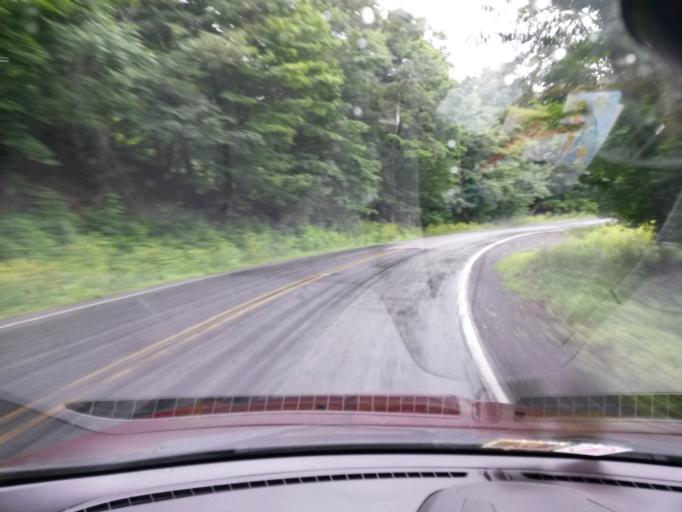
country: US
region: Virginia
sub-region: Highland County
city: Monterey
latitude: 38.4277
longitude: -79.6055
